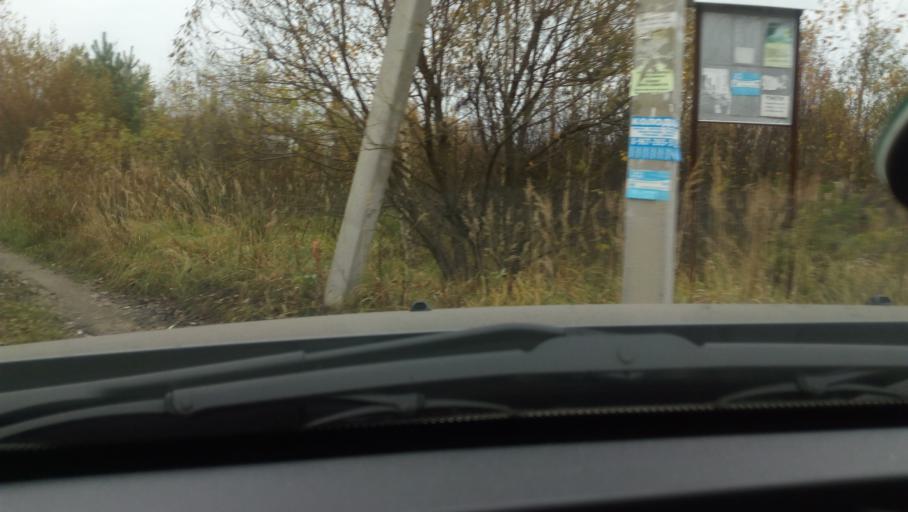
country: RU
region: Moskovskaya
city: Avsyunino
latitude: 55.5800
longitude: 39.2479
